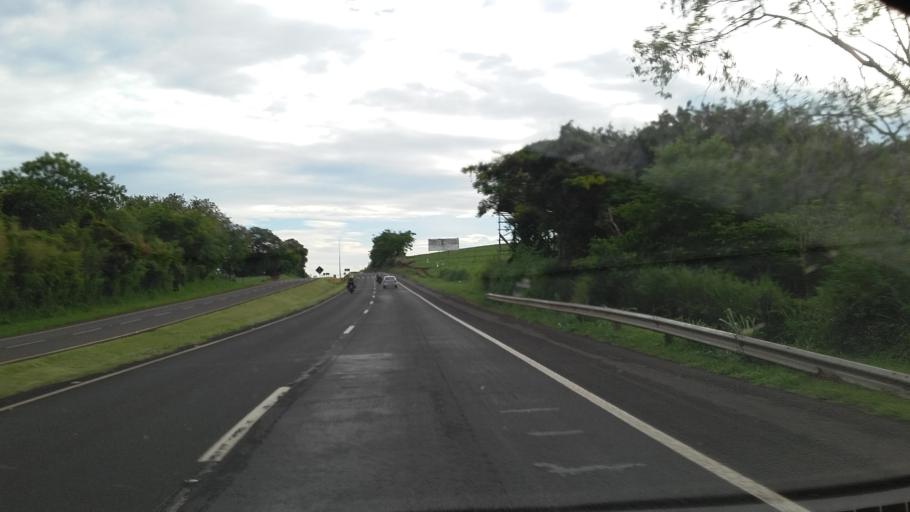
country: BR
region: Parana
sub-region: Paicandu
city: Paicandu
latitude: -23.5133
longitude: -52.0258
